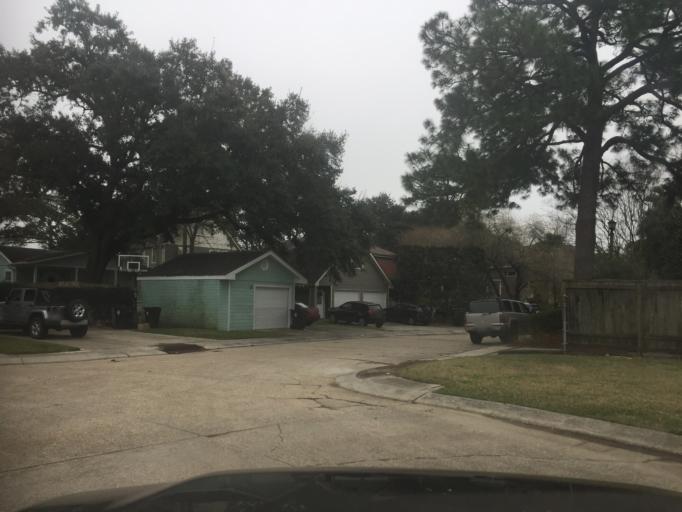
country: US
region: Louisiana
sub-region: Orleans Parish
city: New Orleans
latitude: 30.0206
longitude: -90.0938
